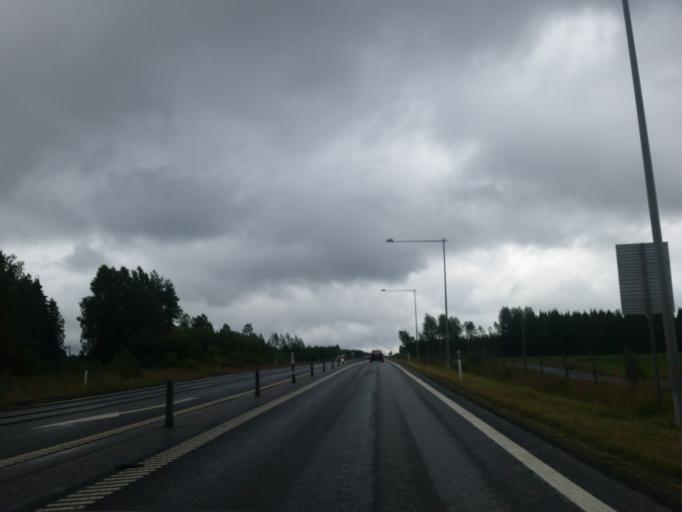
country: SE
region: Vaesterbotten
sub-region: Umea Kommun
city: Ersmark
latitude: 63.8568
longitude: 20.3926
